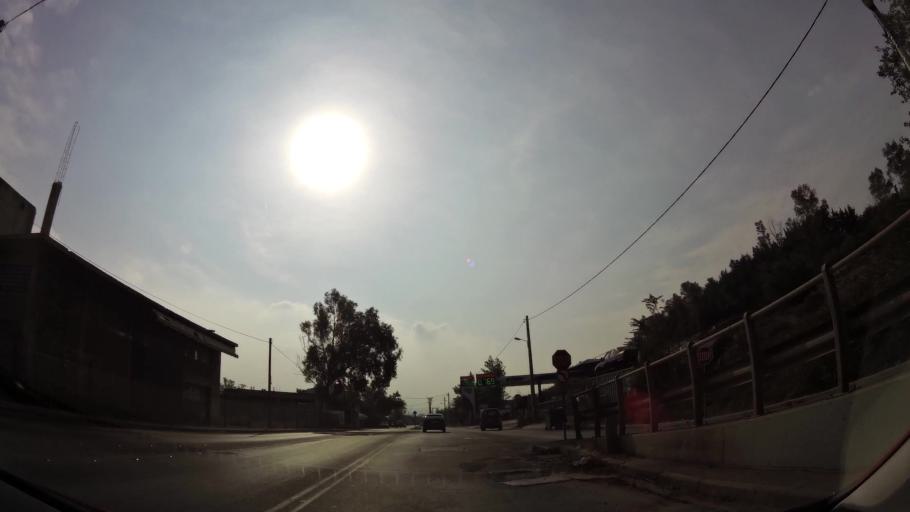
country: GR
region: Attica
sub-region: Nomarchia Dytikis Attikis
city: Zefyri
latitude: 38.0673
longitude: 23.7121
